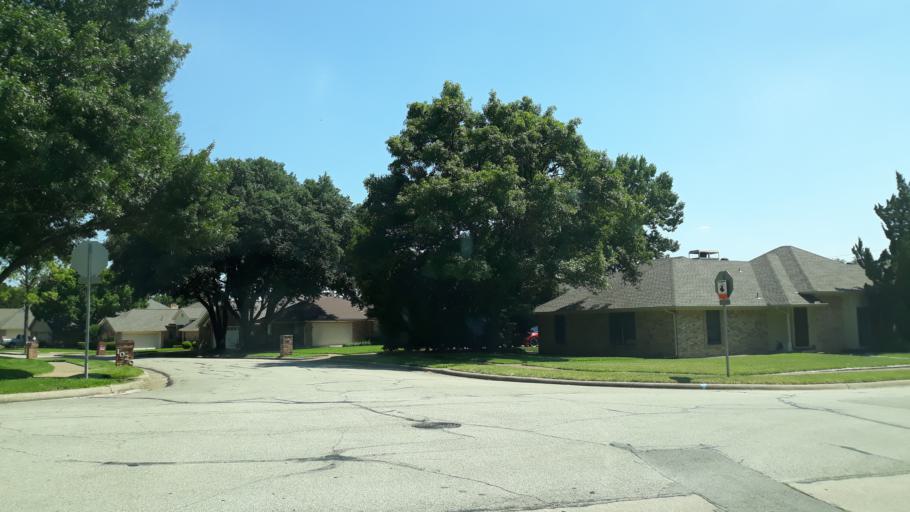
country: US
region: Texas
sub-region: Dallas County
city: Irving
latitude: 32.8247
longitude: -97.0082
